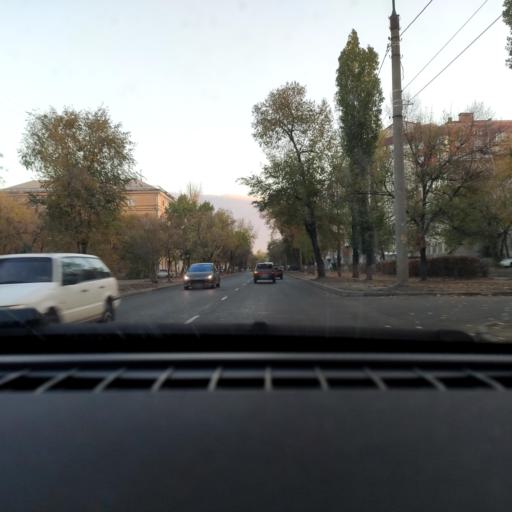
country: RU
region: Voronezj
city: Voronezh
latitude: 51.6359
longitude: 39.2377
